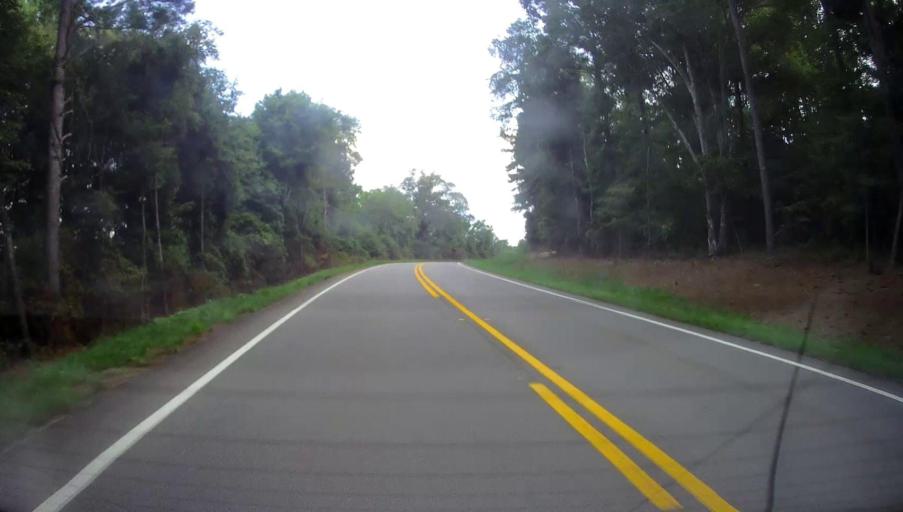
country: US
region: Georgia
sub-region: Monroe County
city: Forsyth
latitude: 33.0049
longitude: -83.9398
